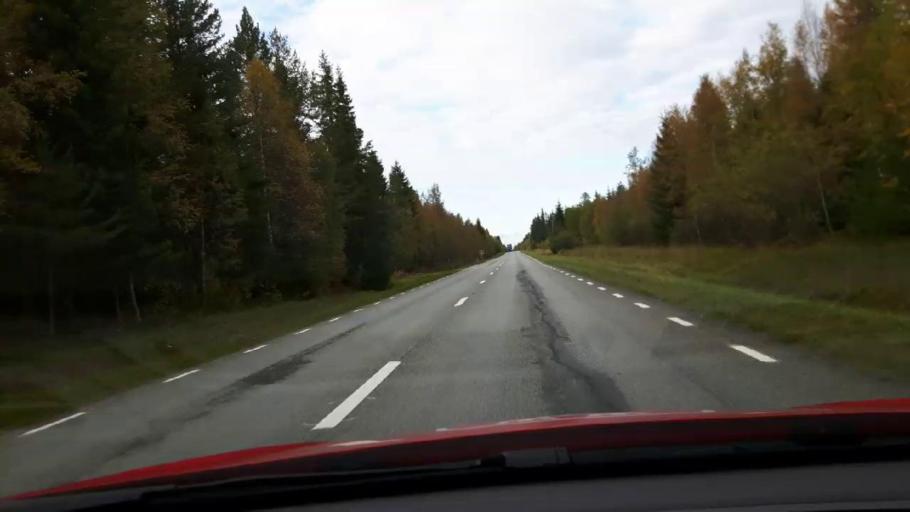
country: SE
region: Jaemtland
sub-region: Krokoms Kommun
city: Valla
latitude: 63.2269
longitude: 14.0161
